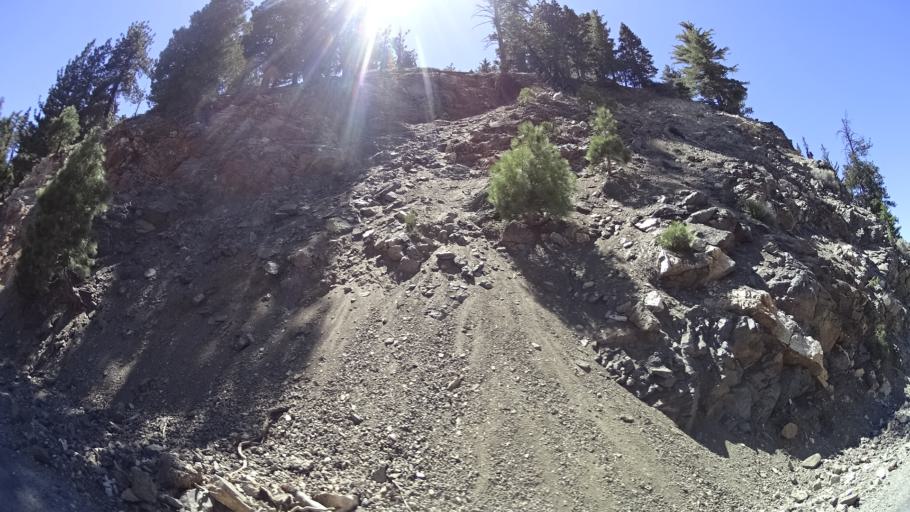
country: US
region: California
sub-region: San Bernardino County
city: Wrightwood
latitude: 34.3472
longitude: -117.8279
